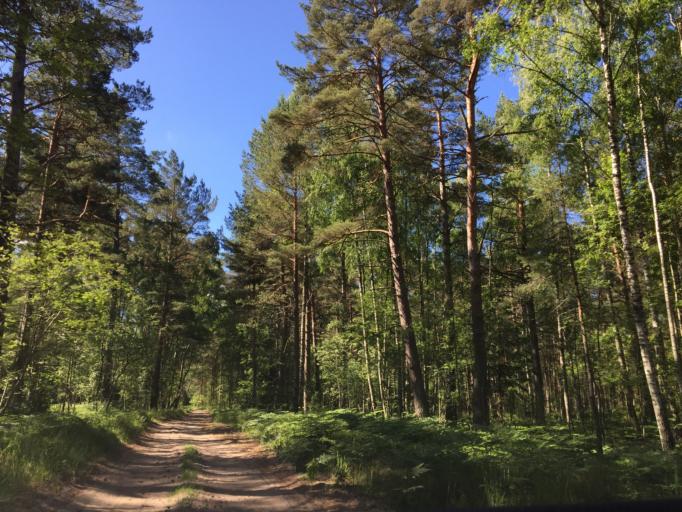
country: LV
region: Ventspils
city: Ventspils
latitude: 57.4596
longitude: 21.6347
